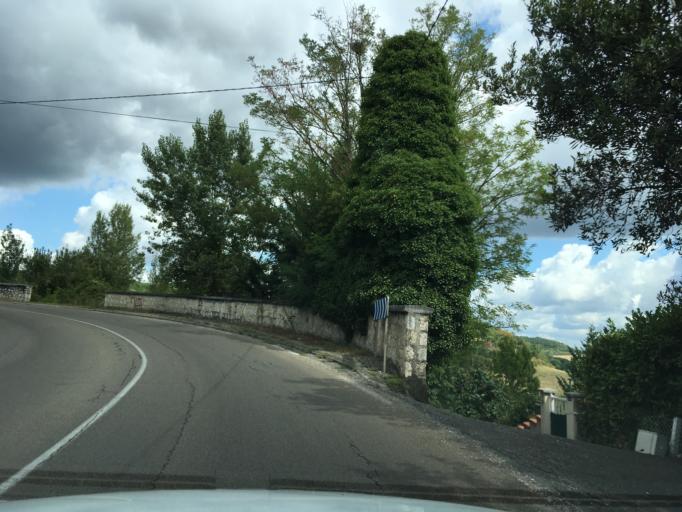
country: FR
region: Aquitaine
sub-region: Departement du Lot-et-Garonne
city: Agen
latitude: 44.2148
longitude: 0.6410
